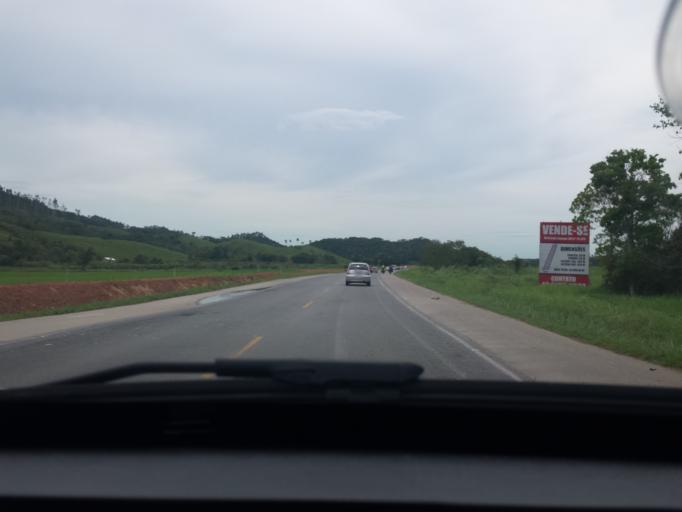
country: BR
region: Santa Catarina
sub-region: Gaspar
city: Gaspar
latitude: -26.8831
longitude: -48.8641
